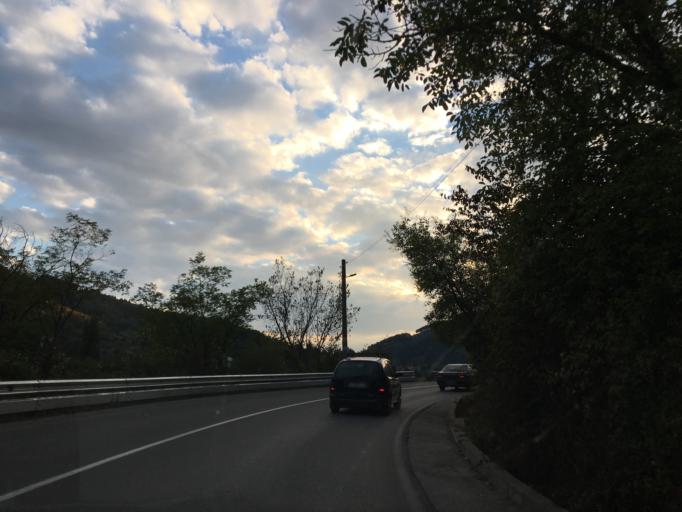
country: BG
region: Sofiya
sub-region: Obshtina Svoge
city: Svoge
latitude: 42.8811
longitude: 23.3908
